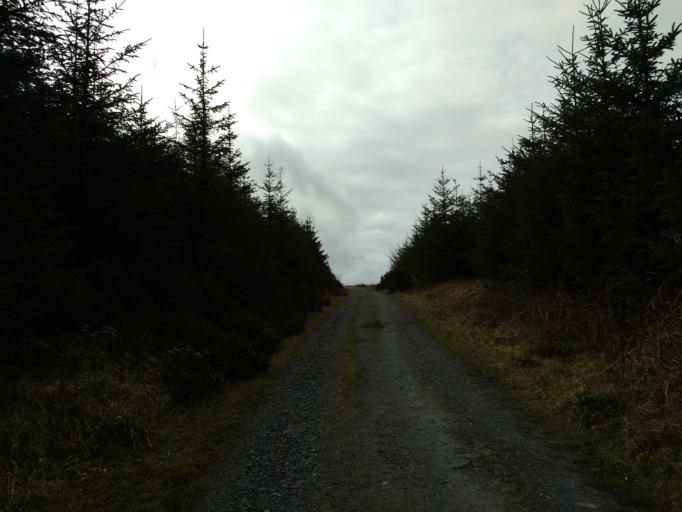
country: IE
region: Leinster
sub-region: Kilkenny
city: Callan
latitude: 52.6656
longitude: -7.5281
